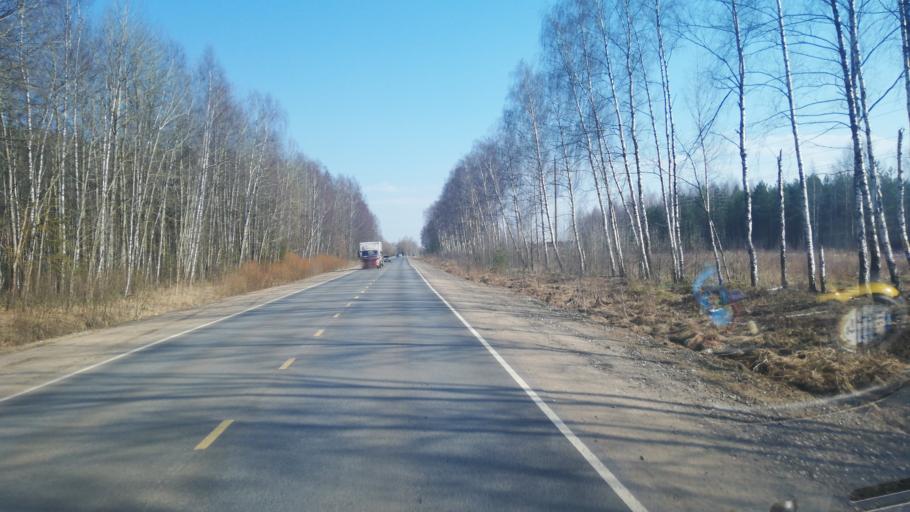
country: RU
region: Jaroslavl
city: Rostov
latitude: 57.2354
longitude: 39.4815
